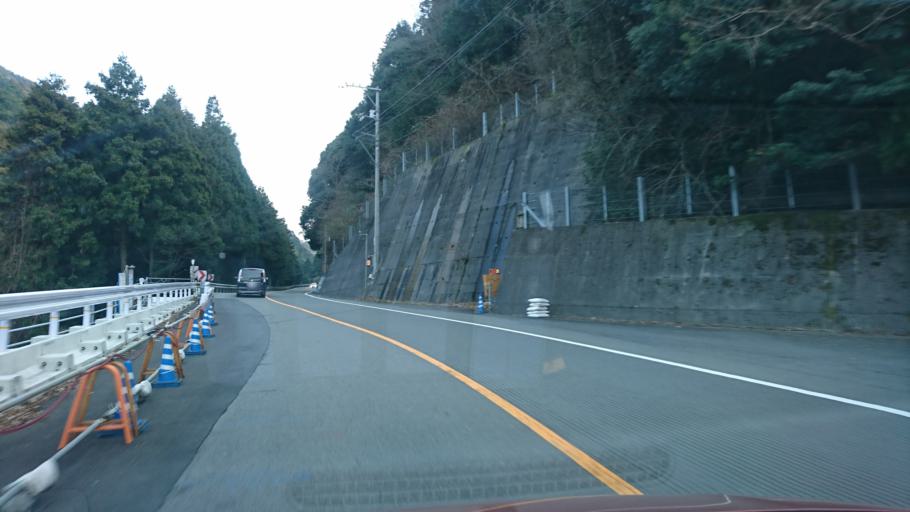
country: JP
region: Ehime
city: Hojo
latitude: 33.9668
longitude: 132.9049
